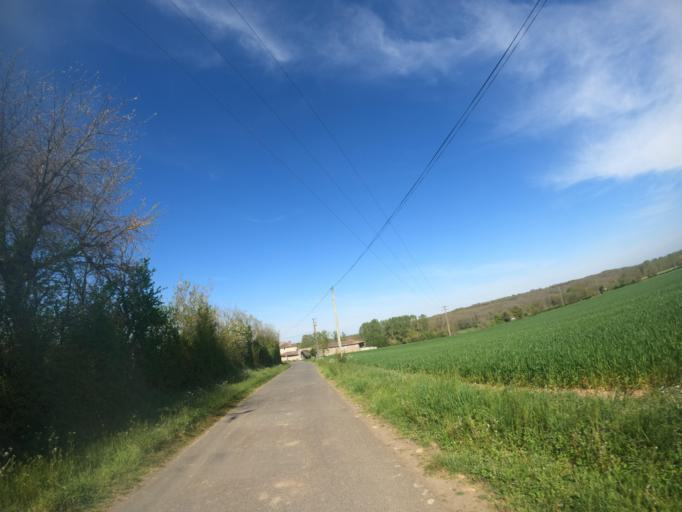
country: FR
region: Poitou-Charentes
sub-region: Departement des Deux-Sevres
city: Saint-Varent
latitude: 46.9068
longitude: -0.2166
